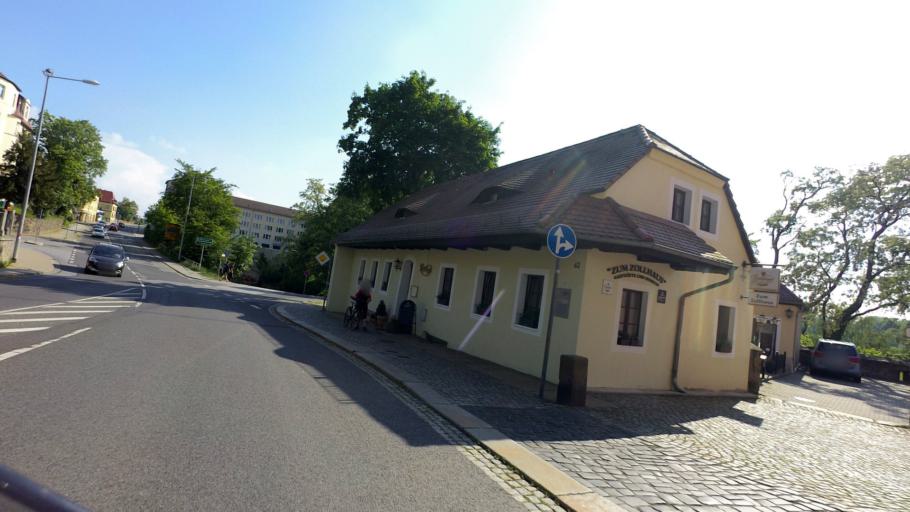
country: DE
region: Saxony
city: Bautzen
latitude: 51.1775
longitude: 14.4232
